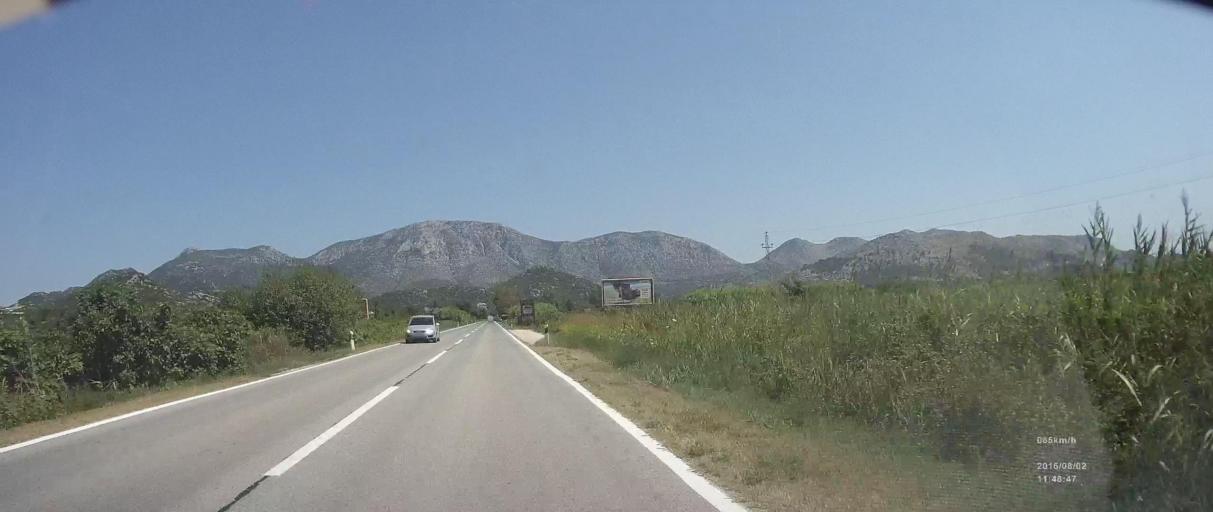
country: HR
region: Dubrovacko-Neretvanska
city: Komin
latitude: 43.0372
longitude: 17.4923
